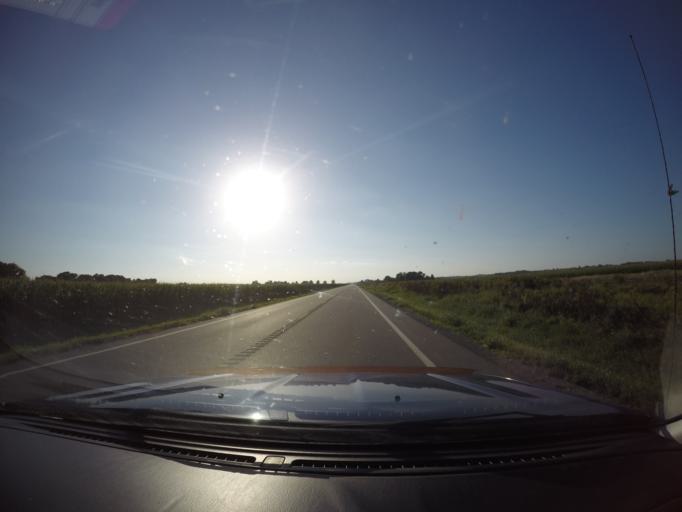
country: US
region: Kansas
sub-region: Shawnee County
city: Rossville
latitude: 39.1547
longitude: -95.9871
